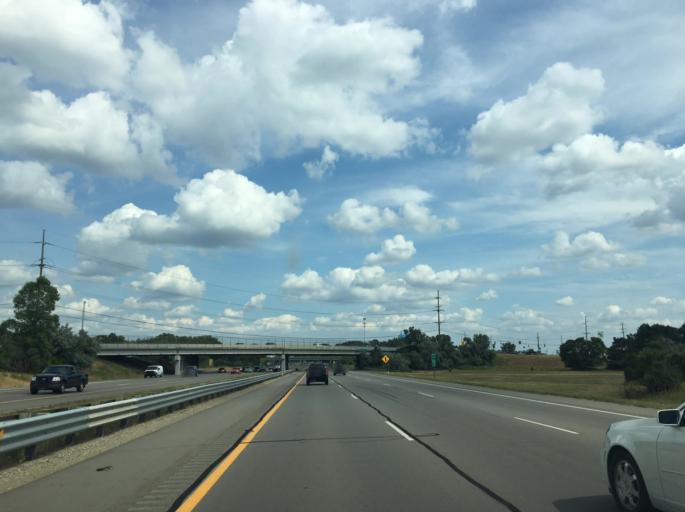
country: US
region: Michigan
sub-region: Oakland County
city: Clarkston
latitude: 42.7372
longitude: -83.3818
